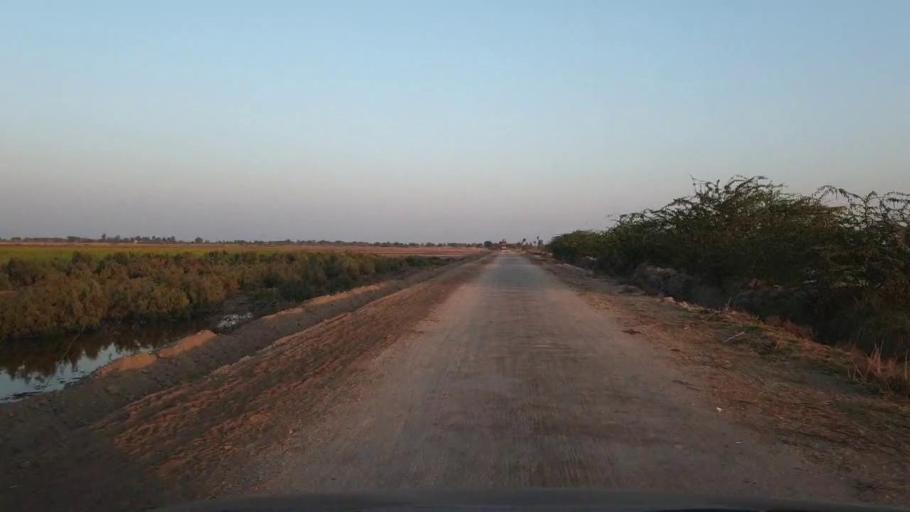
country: PK
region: Sindh
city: Digri
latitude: 25.1385
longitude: 69.2478
